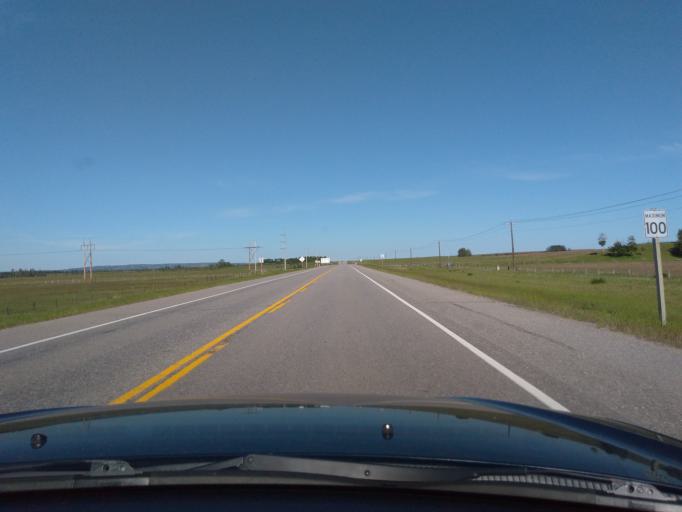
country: CA
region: Alberta
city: Cochrane
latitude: 51.0235
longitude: -114.4594
